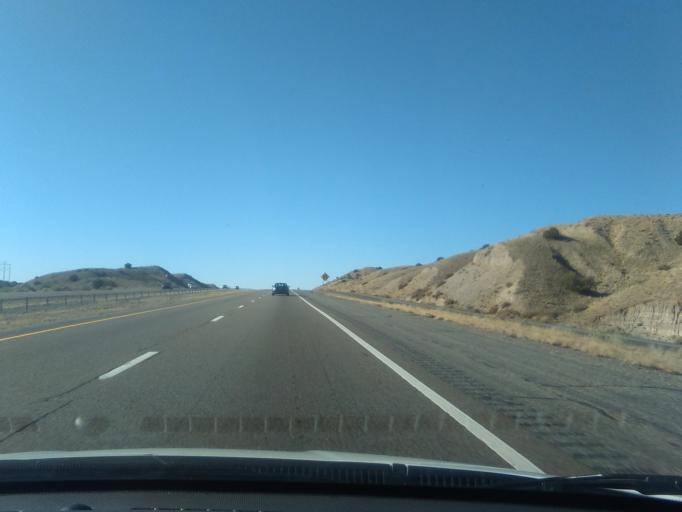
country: US
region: New Mexico
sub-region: Sandoval County
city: San Felipe Pueblo
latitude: 35.4164
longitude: -106.4080
